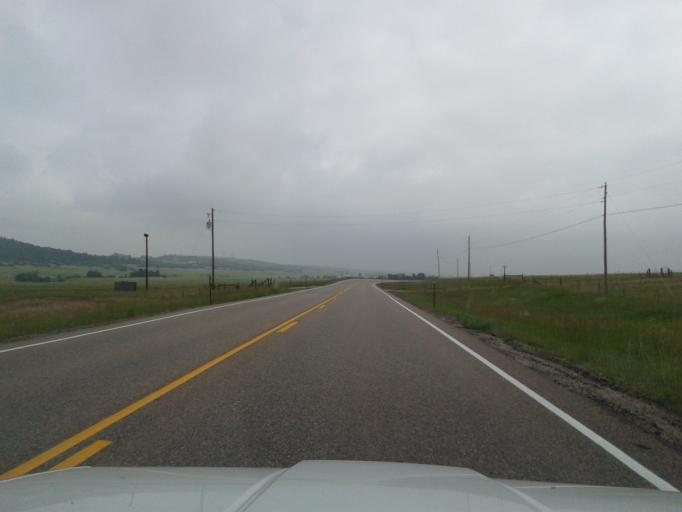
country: US
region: Colorado
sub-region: El Paso County
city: Woodmoor
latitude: 39.1873
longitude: -104.7307
